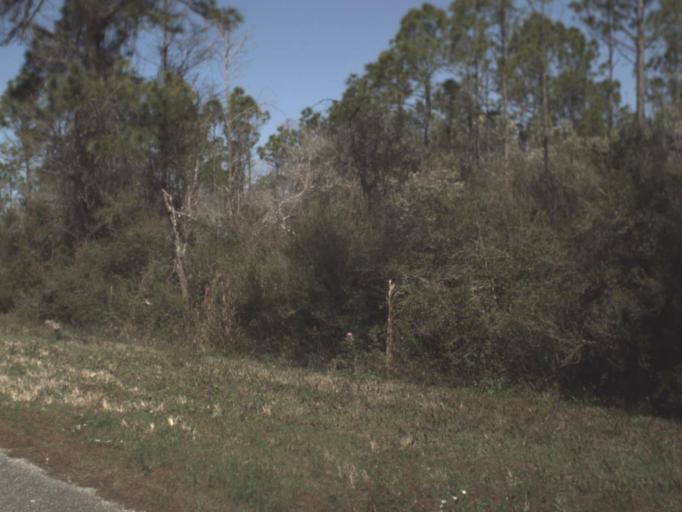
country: US
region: Florida
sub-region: Gulf County
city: Port Saint Joe
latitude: 29.7434
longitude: -85.2311
